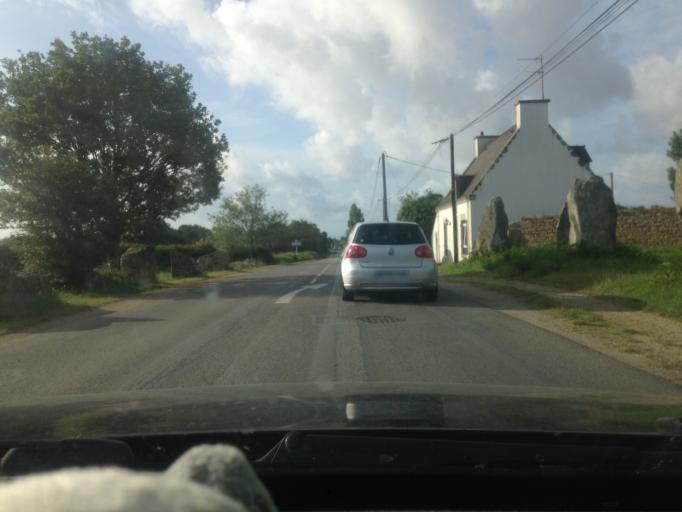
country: FR
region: Brittany
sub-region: Departement du Morbihan
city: Erdeven
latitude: 47.6347
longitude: -3.1492
